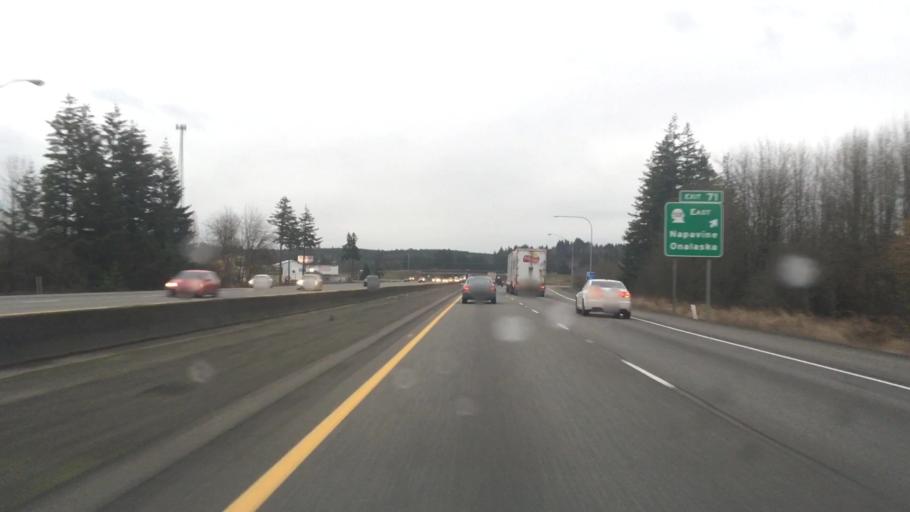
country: US
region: Washington
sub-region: Lewis County
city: Napavine
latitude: 46.5882
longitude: -122.8930
